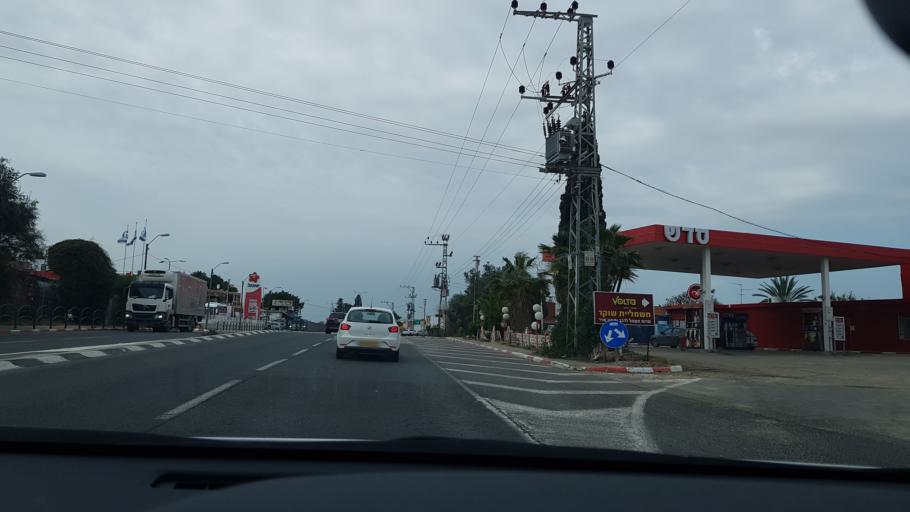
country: IL
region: Central District
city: Gedera
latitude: 31.8176
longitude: 34.7726
